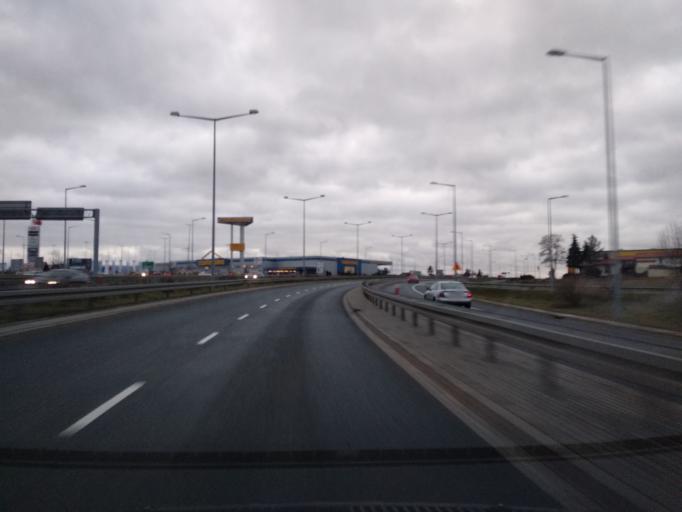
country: PL
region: Greater Poland Voivodeship
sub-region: Powiat koninski
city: Stare Miasto
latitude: 52.1872
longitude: 18.2288
